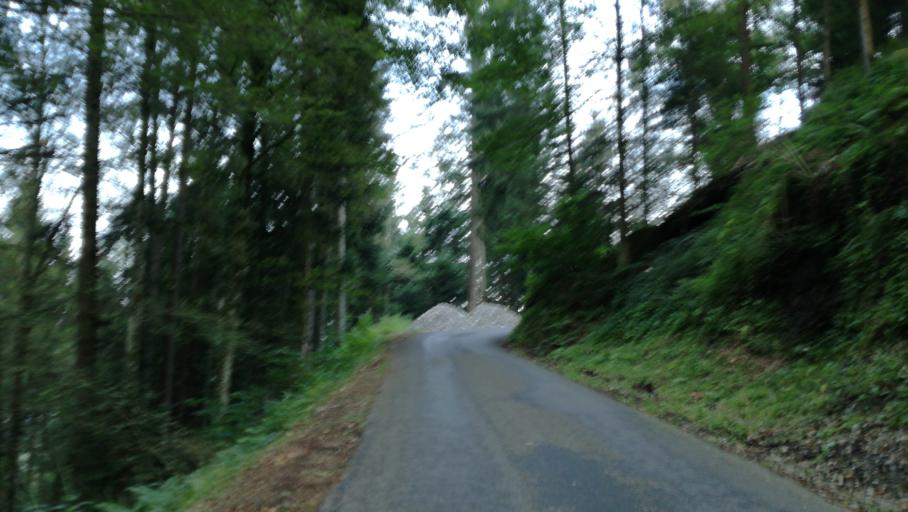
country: CH
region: Zug
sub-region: Zug
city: Zug
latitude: 47.1454
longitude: 8.5450
